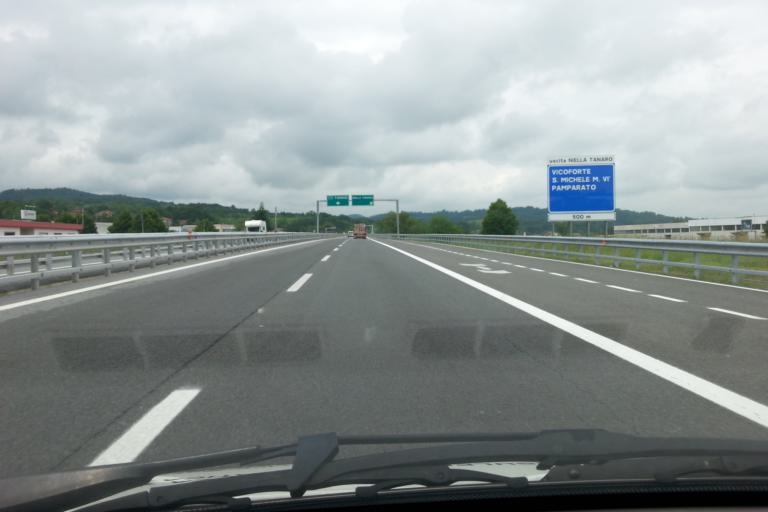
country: IT
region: Piedmont
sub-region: Provincia di Cuneo
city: Borgo
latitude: 44.4064
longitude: 7.9406
